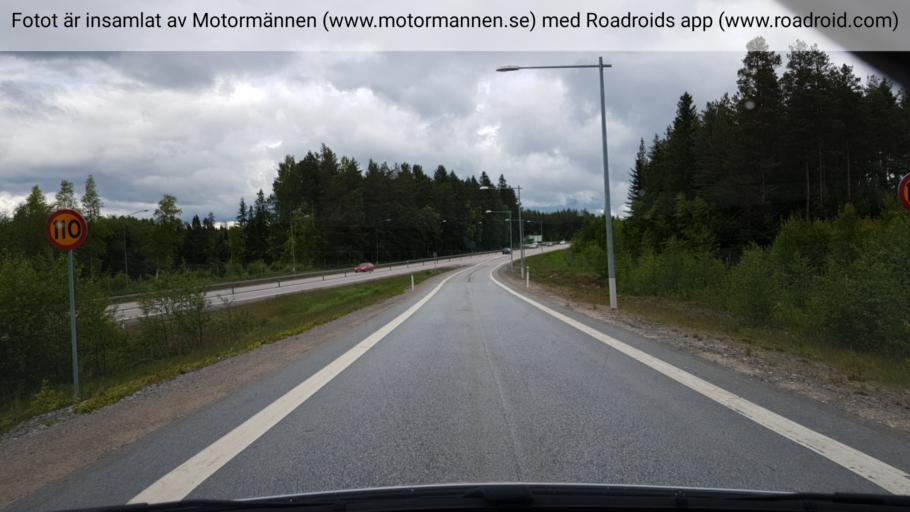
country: SE
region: Vaesterbotten
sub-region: Nordmalings Kommun
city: Nordmaling
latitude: 63.5498
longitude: 19.4159
